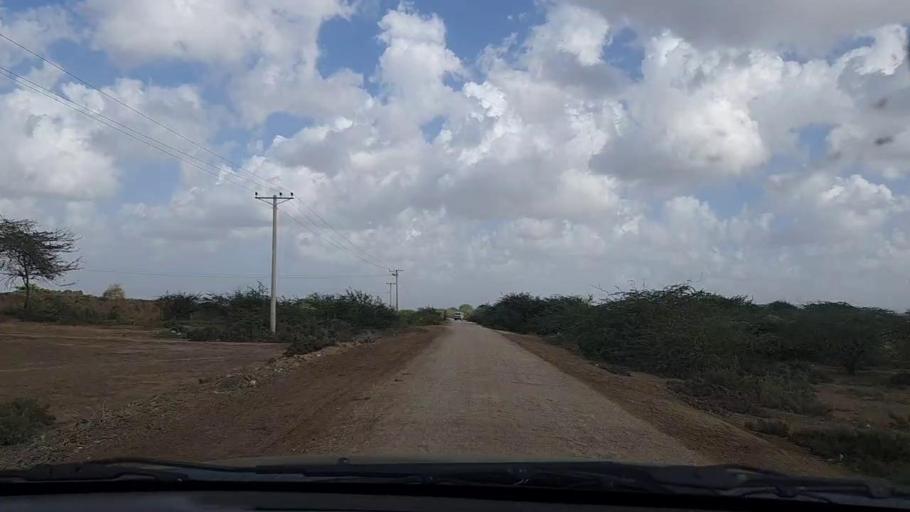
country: PK
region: Sindh
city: Keti Bandar
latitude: 24.1000
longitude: 67.5992
